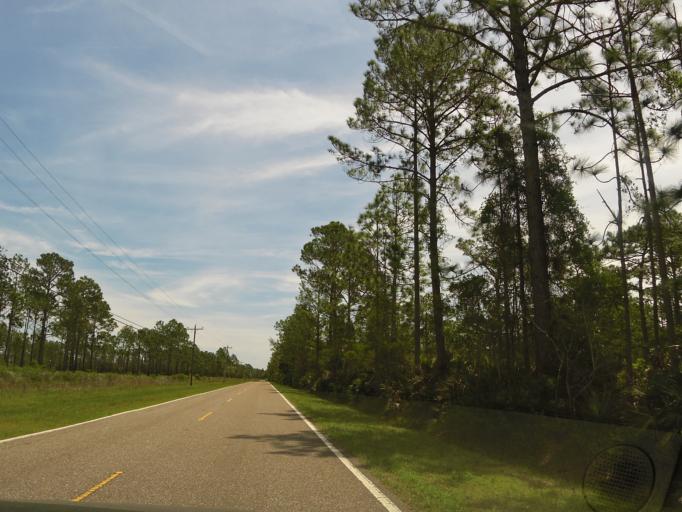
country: US
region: Florida
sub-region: Duval County
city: Atlantic Beach
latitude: 30.4605
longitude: -81.5015
